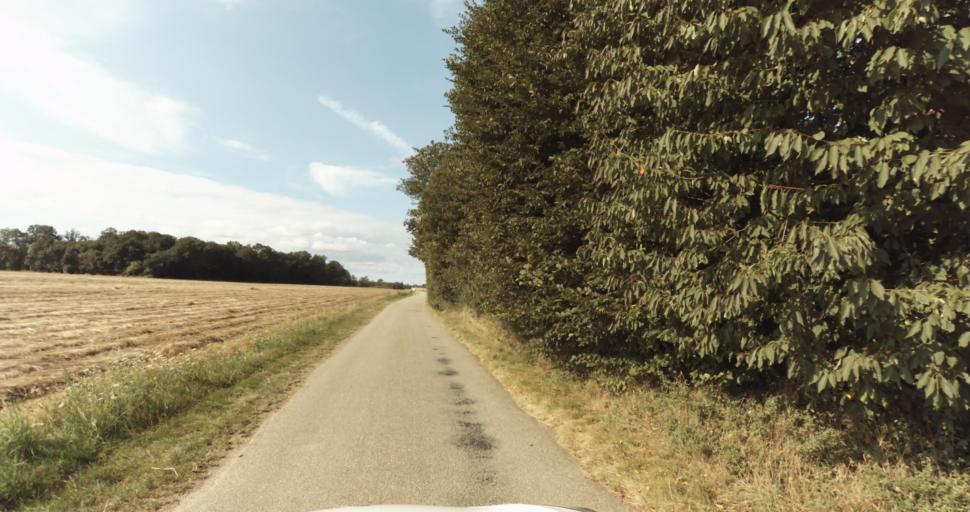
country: FR
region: Haute-Normandie
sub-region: Departement de l'Eure
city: Tillieres-sur-Avre
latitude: 48.7875
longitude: 1.0856
